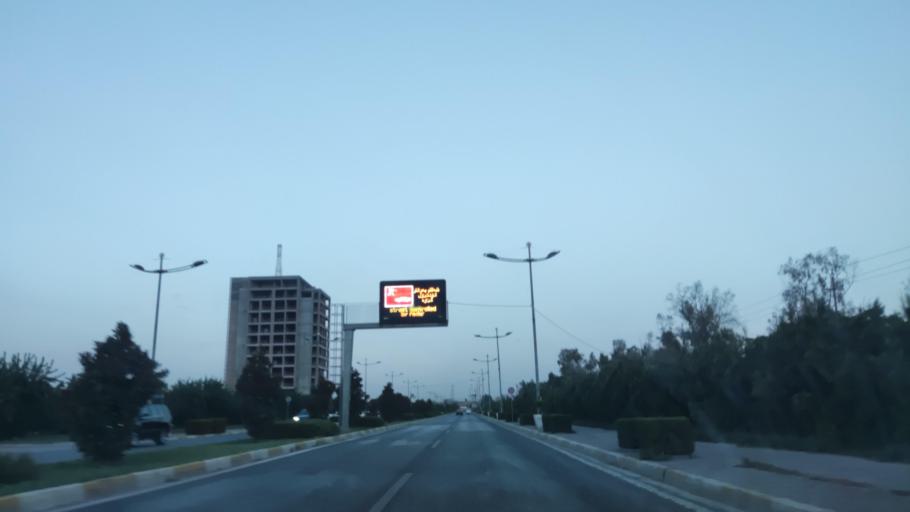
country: IQ
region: Arbil
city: Erbil
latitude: 36.1988
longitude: 43.9837
